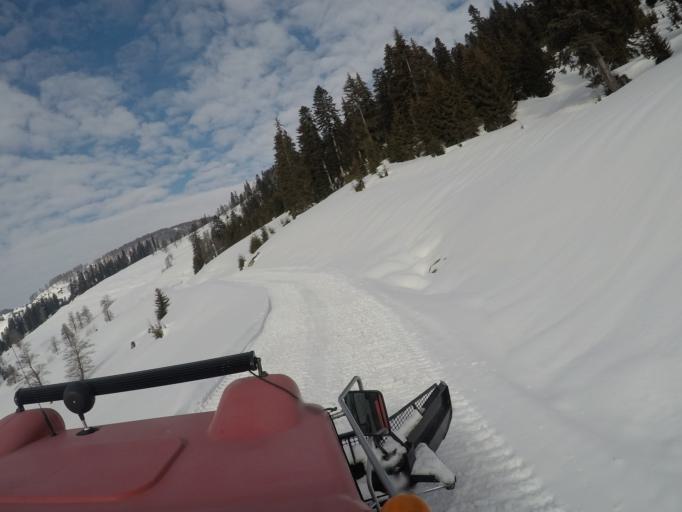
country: GE
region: Samtskhe-Javakheti
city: Adigeni
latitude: 41.6331
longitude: 42.5586
